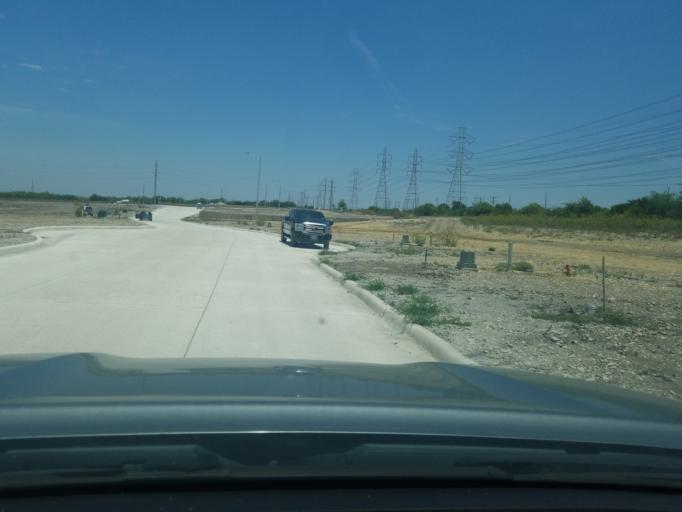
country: US
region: Texas
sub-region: Bexar County
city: Converse
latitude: 29.4654
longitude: -98.3244
